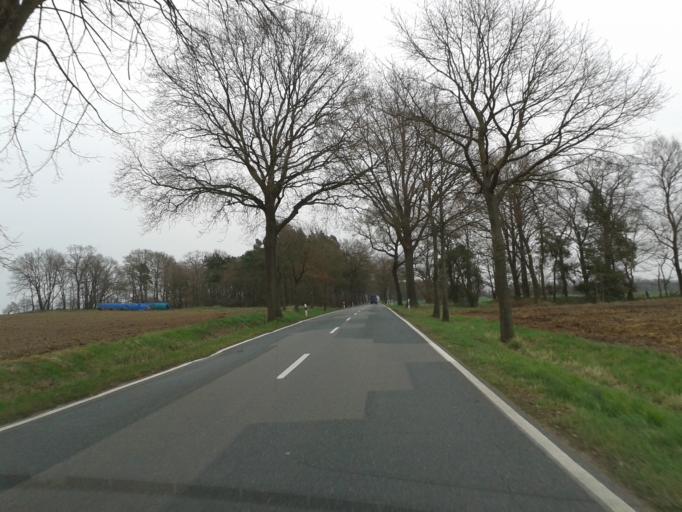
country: DE
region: Lower Saxony
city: Trebel
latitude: 52.9100
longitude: 11.3272
